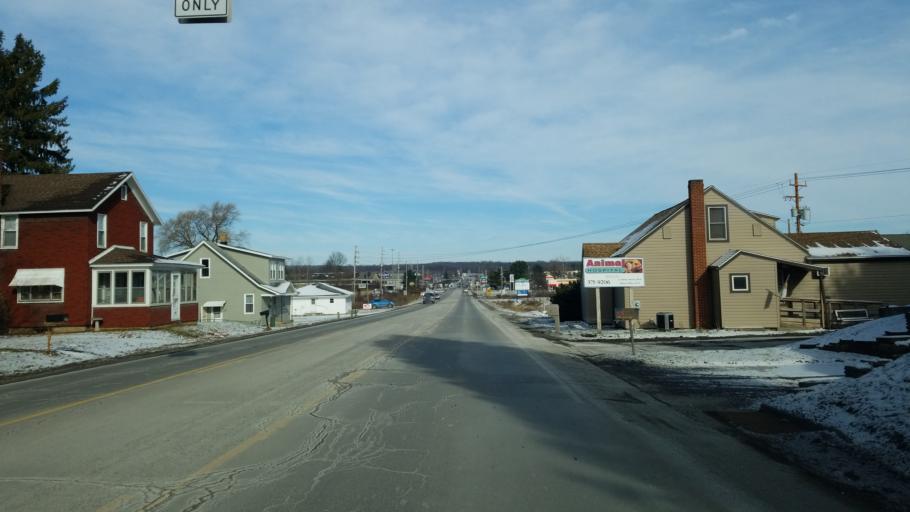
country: US
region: Pennsylvania
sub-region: Clearfield County
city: DuBois
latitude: 41.1151
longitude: -78.7326
